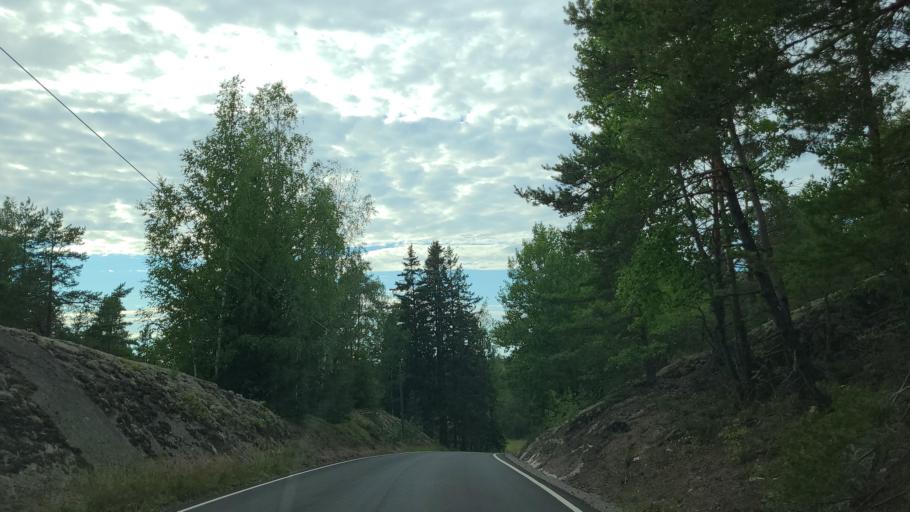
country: FI
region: Varsinais-Suomi
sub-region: Turku
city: Rymaettylae
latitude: 60.3204
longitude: 21.9580
